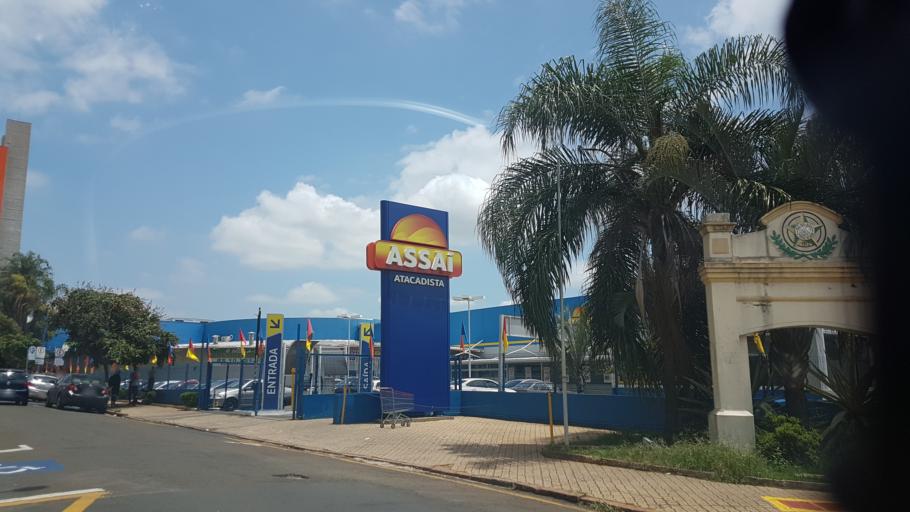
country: BR
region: Sao Paulo
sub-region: Piracicaba
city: Piracicaba
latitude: -22.7216
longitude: -47.6459
